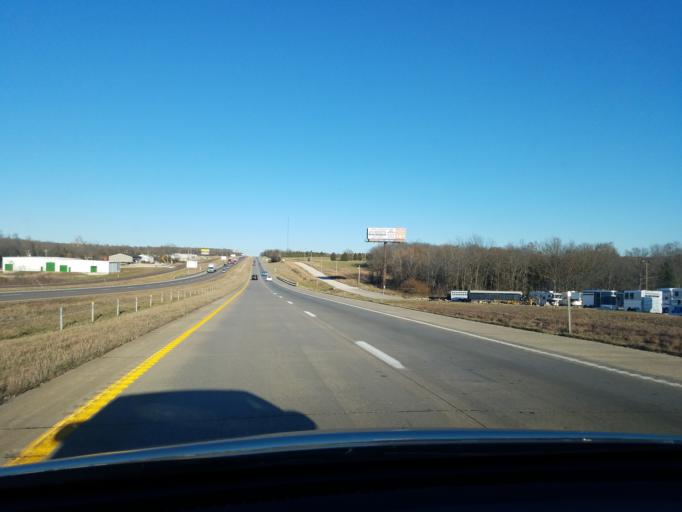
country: US
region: Missouri
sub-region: Crawford County
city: Cuba
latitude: 38.0758
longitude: -91.4012
